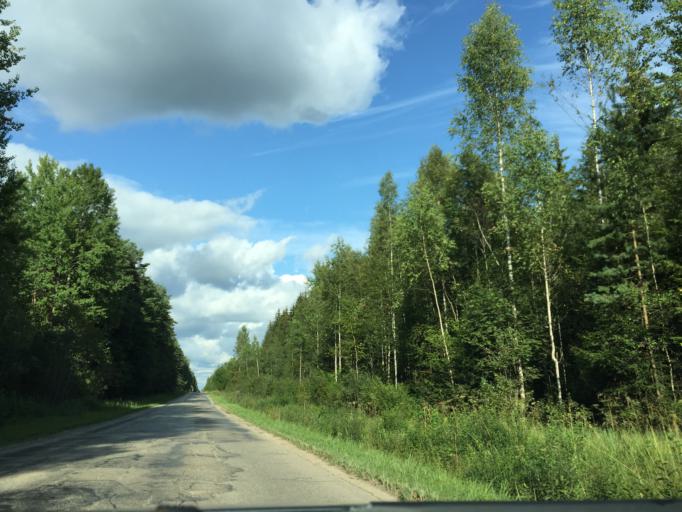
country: LV
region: Ogre
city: Ogre
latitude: 56.8309
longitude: 24.6481
